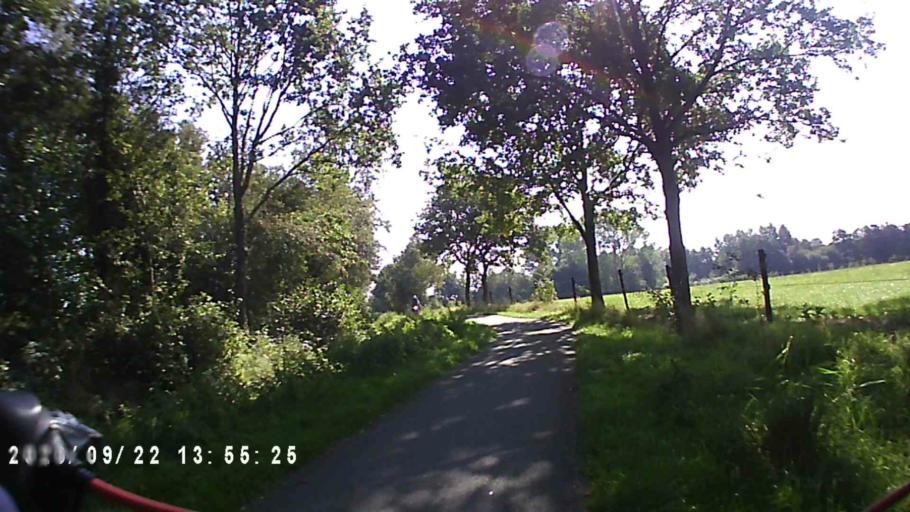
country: NL
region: Groningen
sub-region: Gemeente Leek
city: Leek
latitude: 53.1260
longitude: 6.4205
